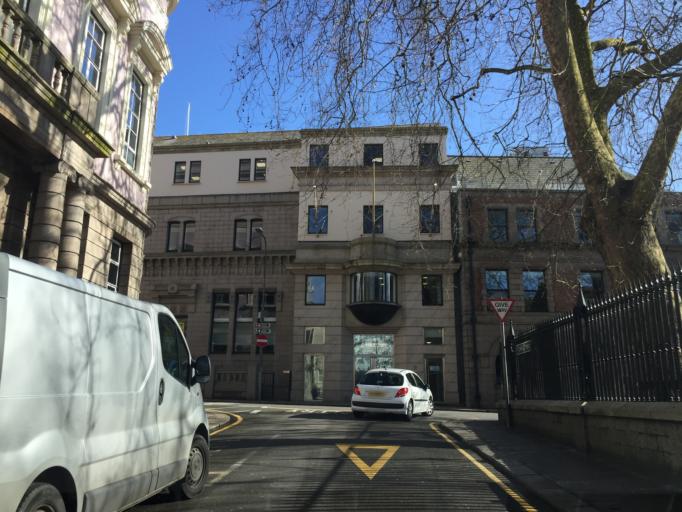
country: JE
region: St Helier
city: Saint Helier
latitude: 49.1837
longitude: -2.1064
